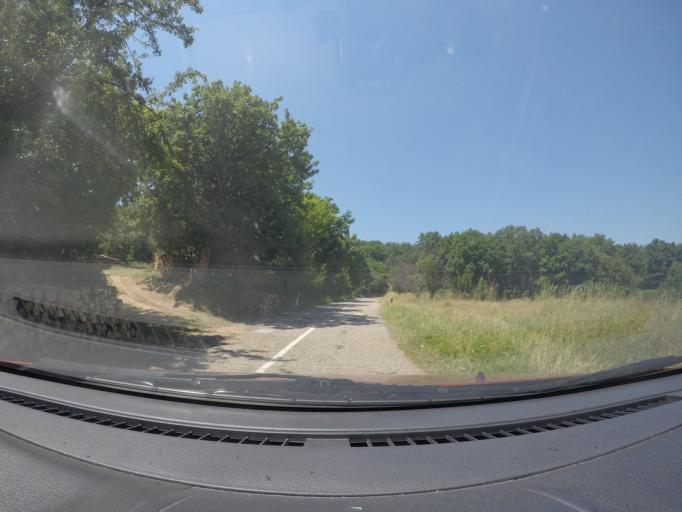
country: RO
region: Mehedinti
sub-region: Comuna Svinita
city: Svinita
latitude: 44.4703
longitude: 22.0964
